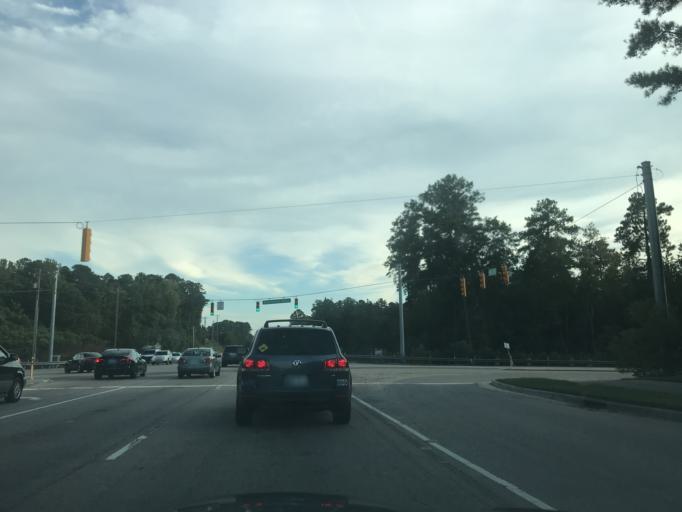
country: US
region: North Carolina
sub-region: Wake County
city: Green Level
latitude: 35.8142
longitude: -78.8729
